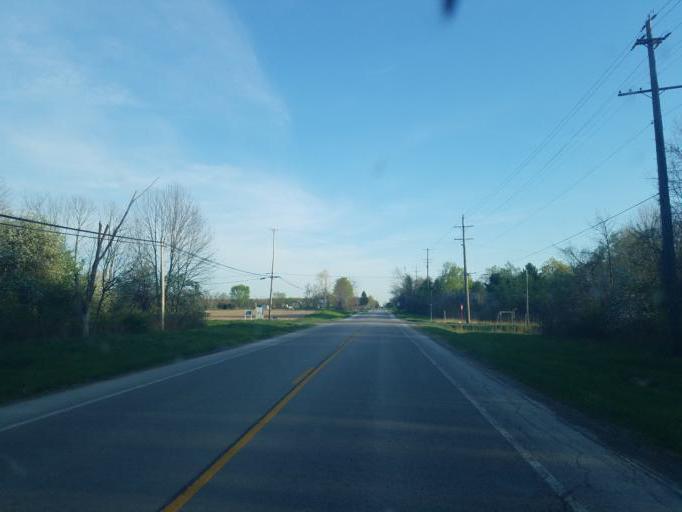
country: US
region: Ohio
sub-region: Ashtabula County
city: Conneaut
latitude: 41.8198
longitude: -80.5723
